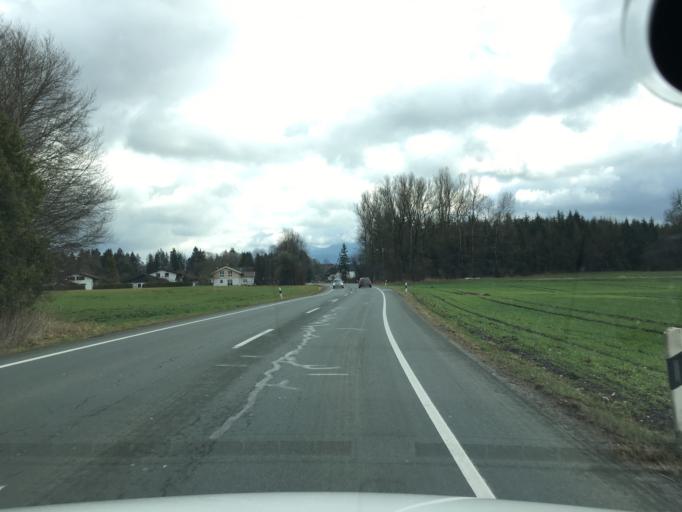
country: DE
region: Bavaria
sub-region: Upper Bavaria
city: Stephanskirchen
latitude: 47.8395
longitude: 12.1680
